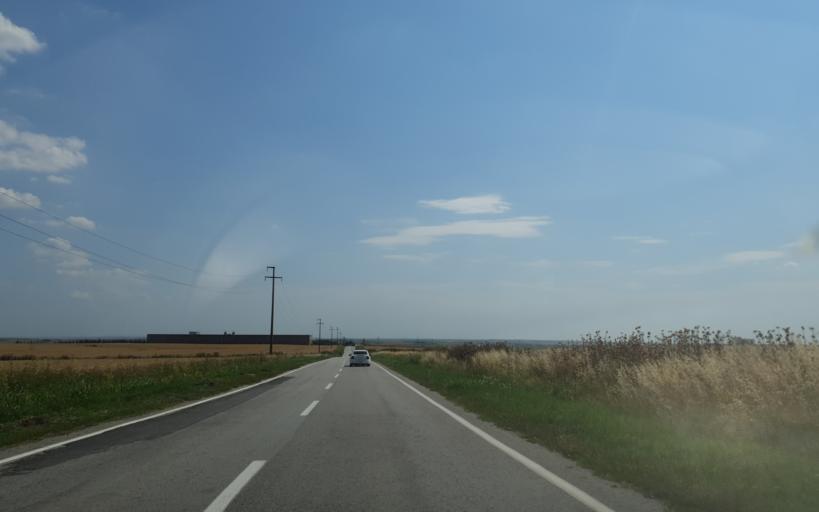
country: TR
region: Kirklareli
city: Buyukkaristiran
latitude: 41.3259
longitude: 27.5276
